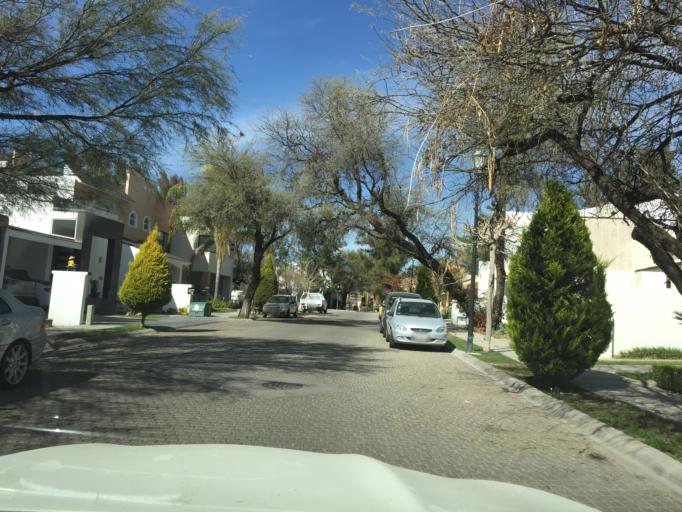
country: MX
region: Aguascalientes
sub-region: Aguascalientes
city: La Loma de los Negritos
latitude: 21.8499
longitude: -102.3554
